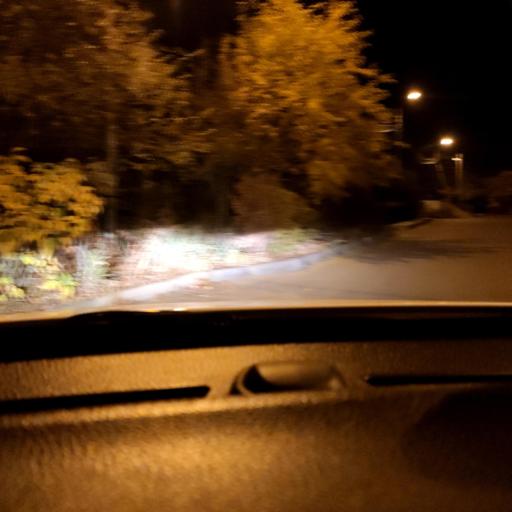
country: RU
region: Voronezj
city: Voronezh
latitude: 51.7233
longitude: 39.2266
